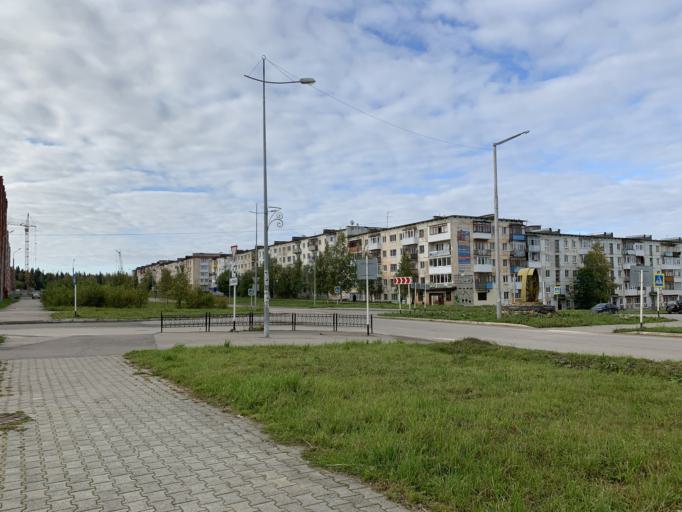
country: RU
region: Perm
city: Gubakha
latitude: 58.8294
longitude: 57.5585
